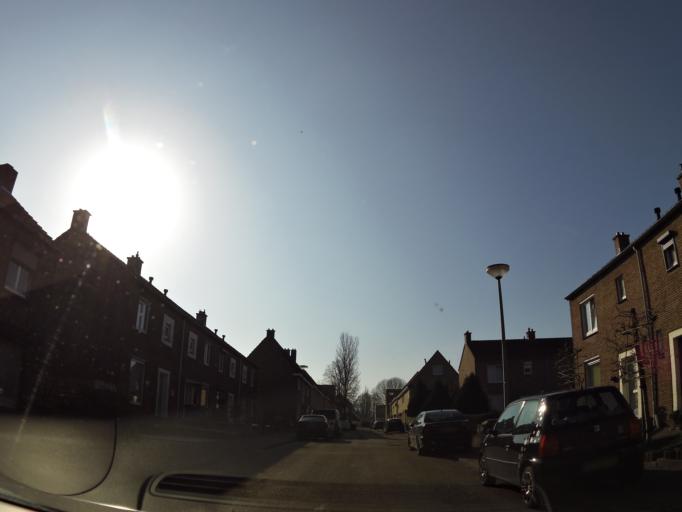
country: NL
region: Limburg
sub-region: Gemeente Kerkrade
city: Kerkrade
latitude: 50.9083
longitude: 6.0326
